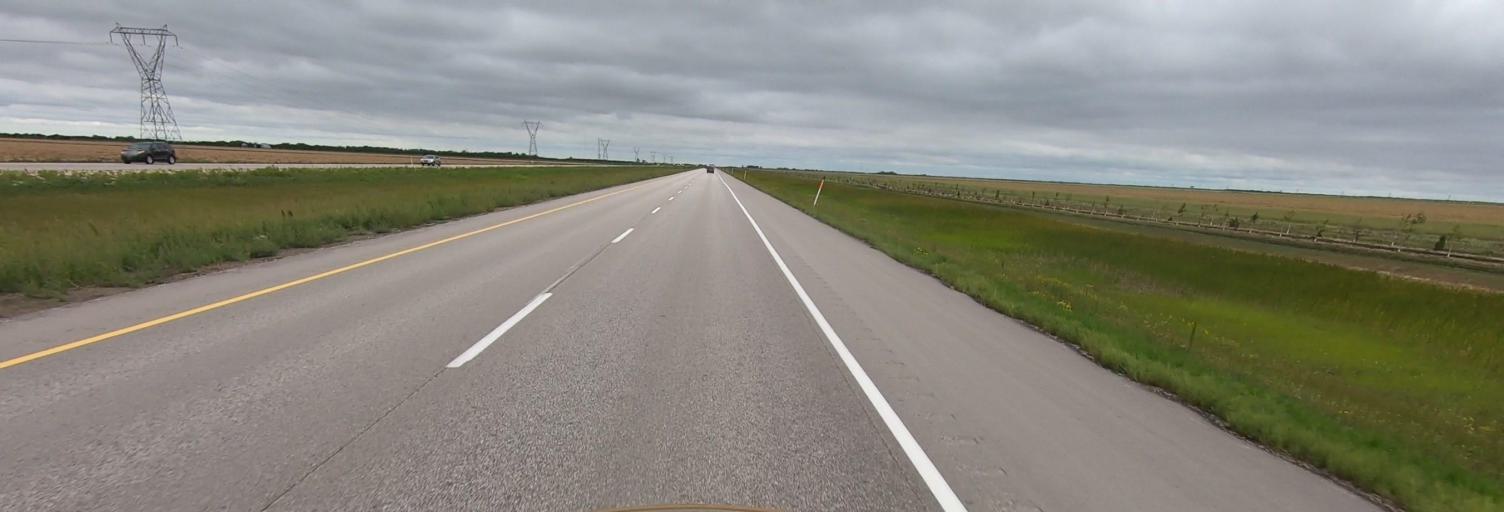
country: CA
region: Manitoba
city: Headingley
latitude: 49.8871
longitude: -97.6044
